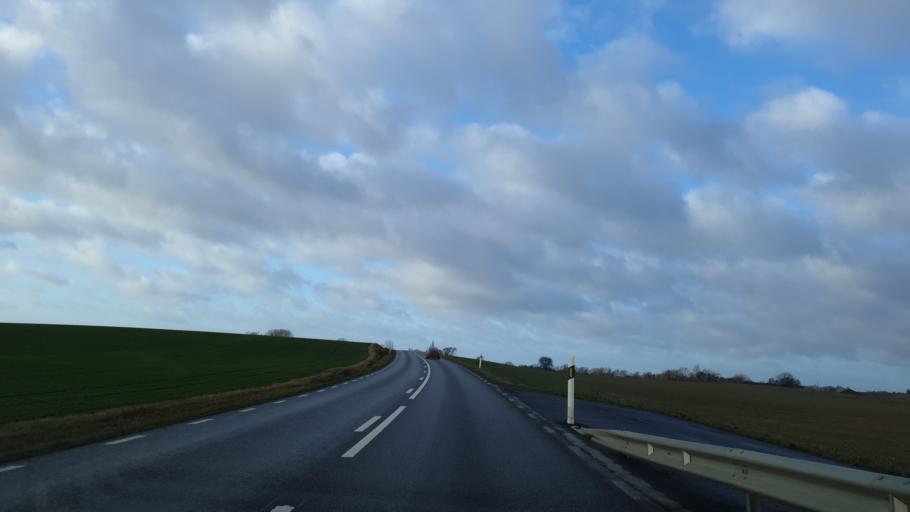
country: SE
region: Skane
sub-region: Trelleborgs Kommun
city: Trelleborg
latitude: 55.4588
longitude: 13.1624
